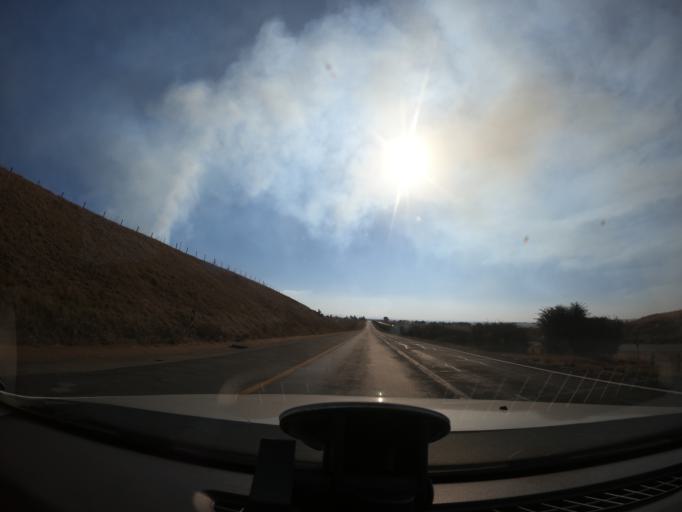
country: ZA
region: Gauteng
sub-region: Sedibeng District Municipality
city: Heidelberg
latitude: -26.4582
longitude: 28.3275
